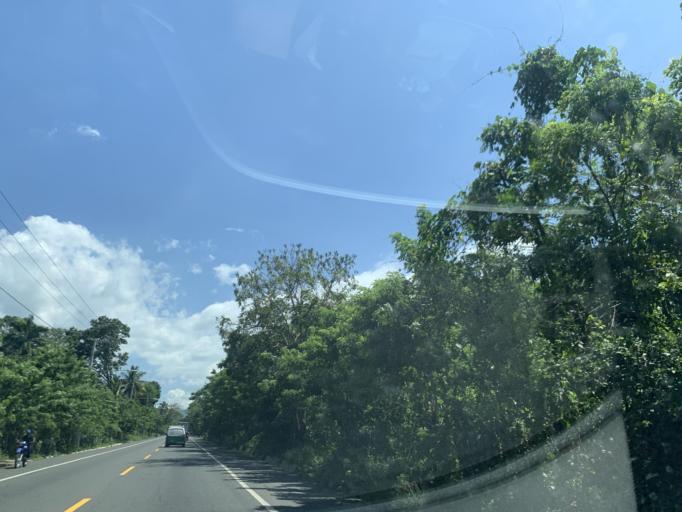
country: DO
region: Puerto Plata
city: Altamira
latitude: 19.7146
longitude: -70.8348
